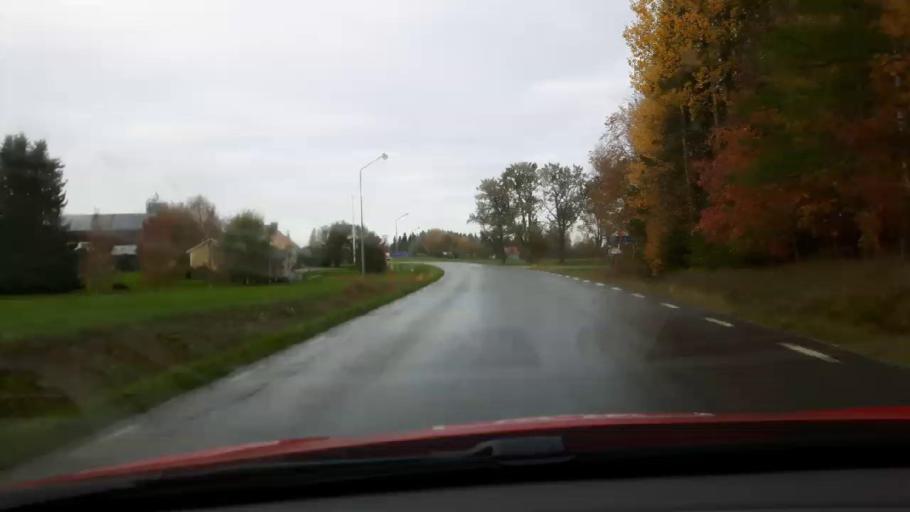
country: SE
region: Jaemtland
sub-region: Bergs Kommun
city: Hoverberg
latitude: 63.0352
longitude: 14.3455
